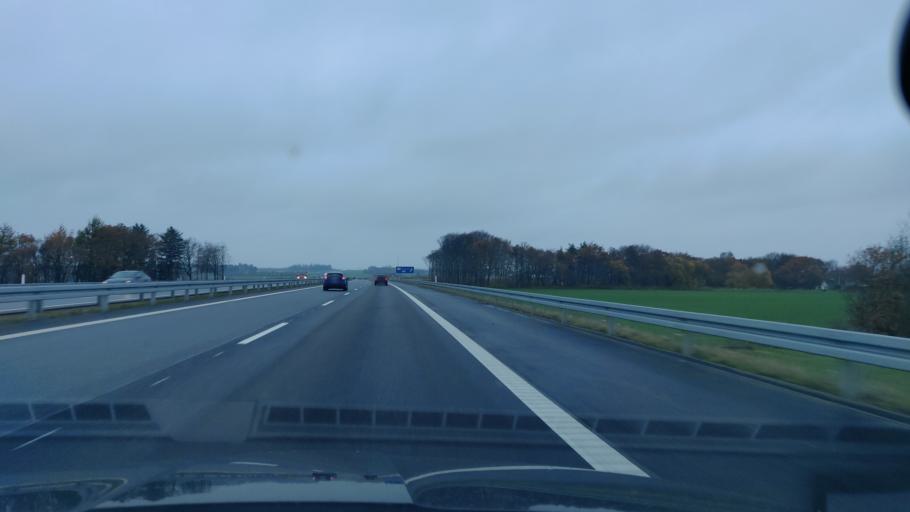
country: DK
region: Central Jutland
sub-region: Herning Kommune
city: Avlum
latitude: 56.2522
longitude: 8.7882
